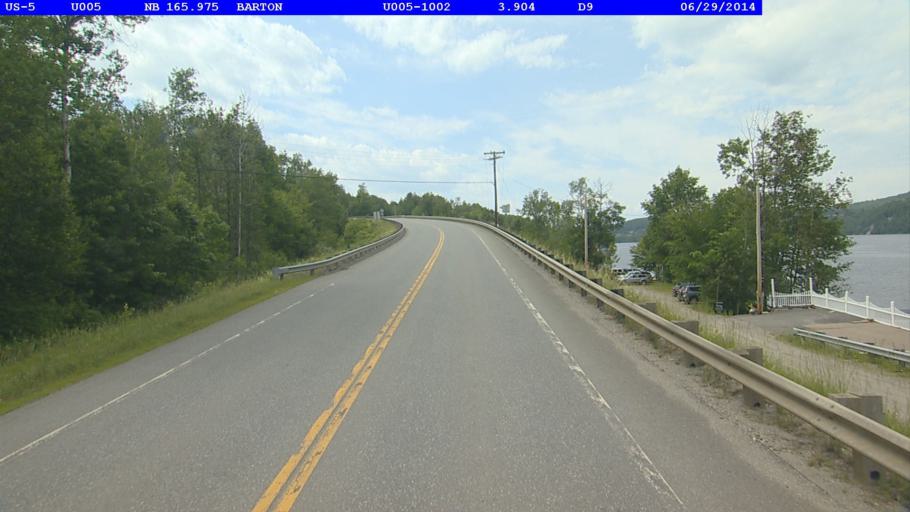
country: US
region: Vermont
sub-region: Orleans County
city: Newport
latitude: 44.7308
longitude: -72.1586
